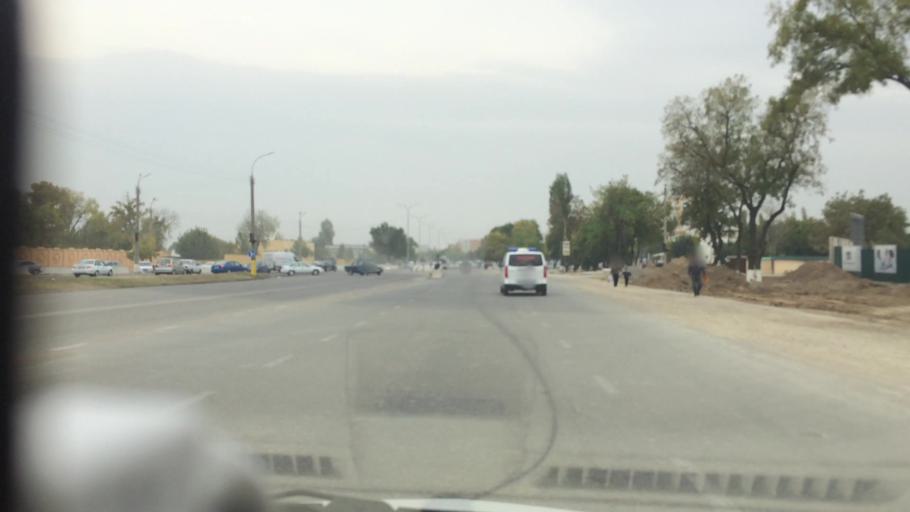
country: UZ
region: Toshkent
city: Salor
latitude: 41.3046
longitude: 69.3412
